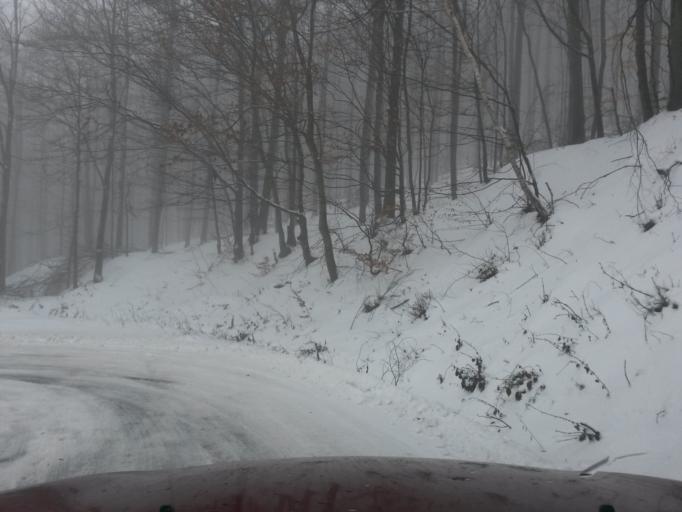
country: SK
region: Presovsky
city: Vranov nad Topl'ou
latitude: 48.8142
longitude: 21.5343
